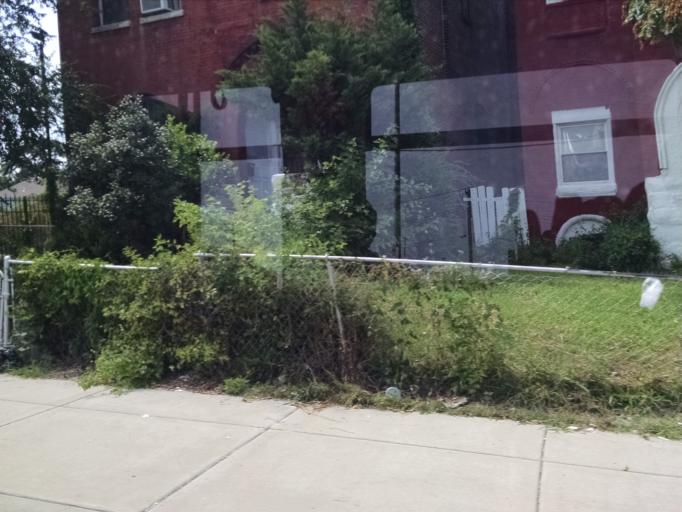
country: US
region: Missouri
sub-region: City of Saint Louis
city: St. Louis
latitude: 38.6452
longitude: -90.2278
